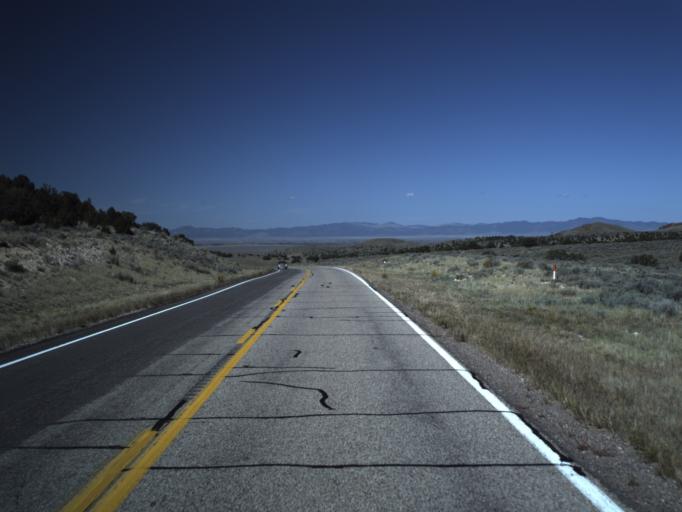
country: US
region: Utah
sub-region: Washington County
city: Enterprise
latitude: 37.6743
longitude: -113.4923
